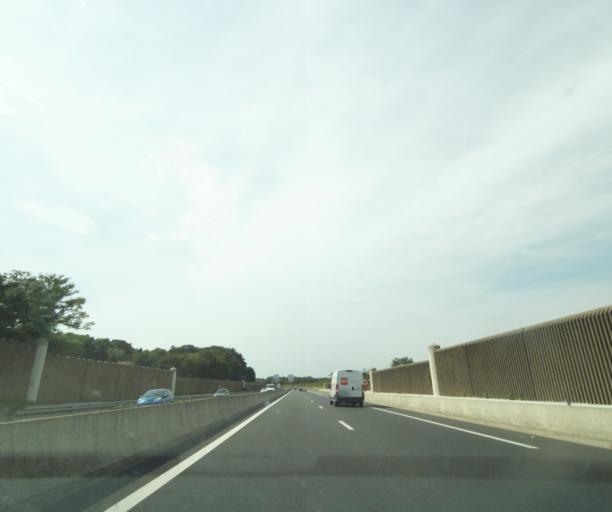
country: FR
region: Centre
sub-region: Departement d'Indre-et-Loire
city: Saint-Cyr-sur-Loire
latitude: 47.4009
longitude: 0.6465
